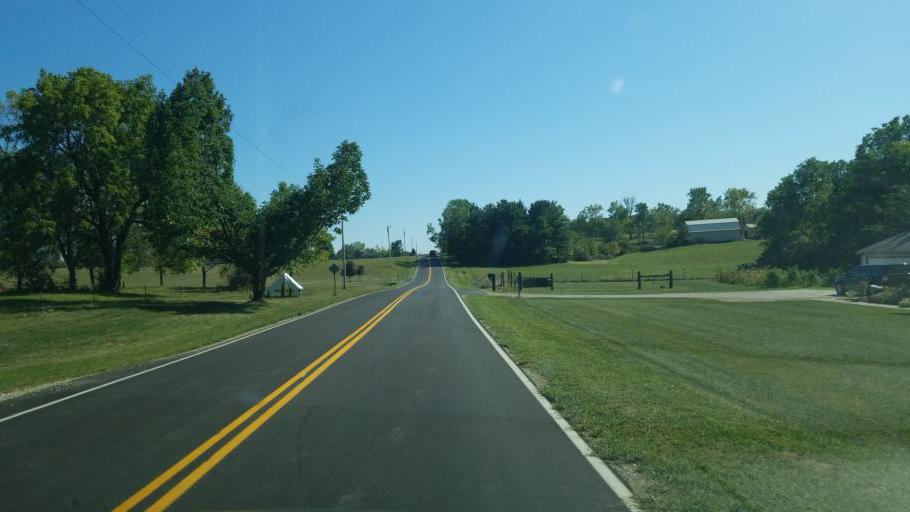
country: US
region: Ohio
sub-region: Champaign County
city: North Lewisburg
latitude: 40.1603
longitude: -83.6033
